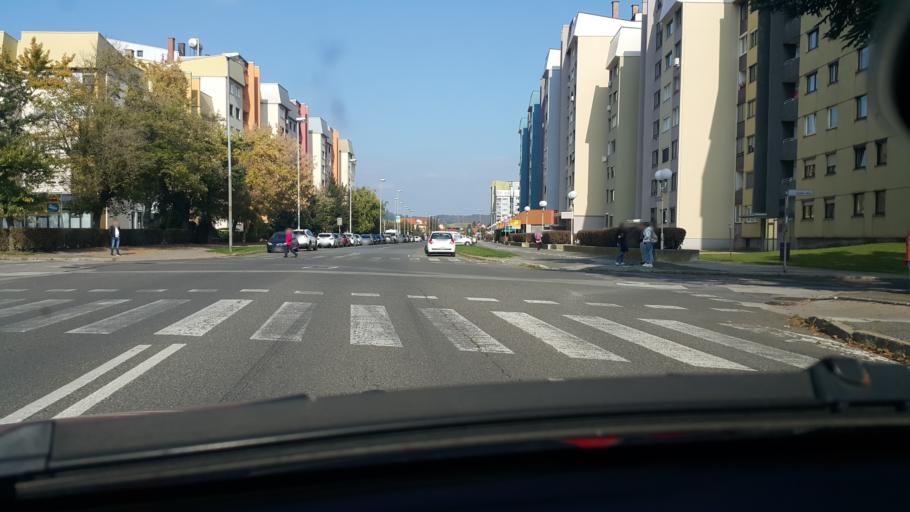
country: SI
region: Maribor
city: Maribor
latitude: 46.5405
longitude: 15.6328
